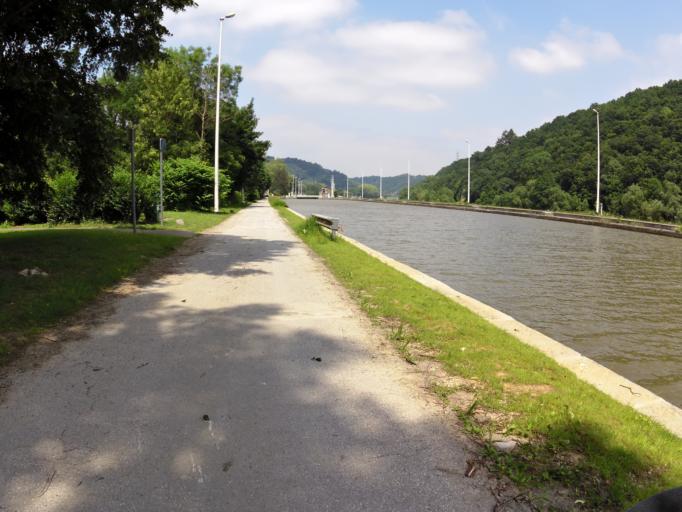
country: BE
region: Wallonia
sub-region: Province de Namur
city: Hastiere-Lavaux
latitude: 50.2010
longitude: 4.8184
